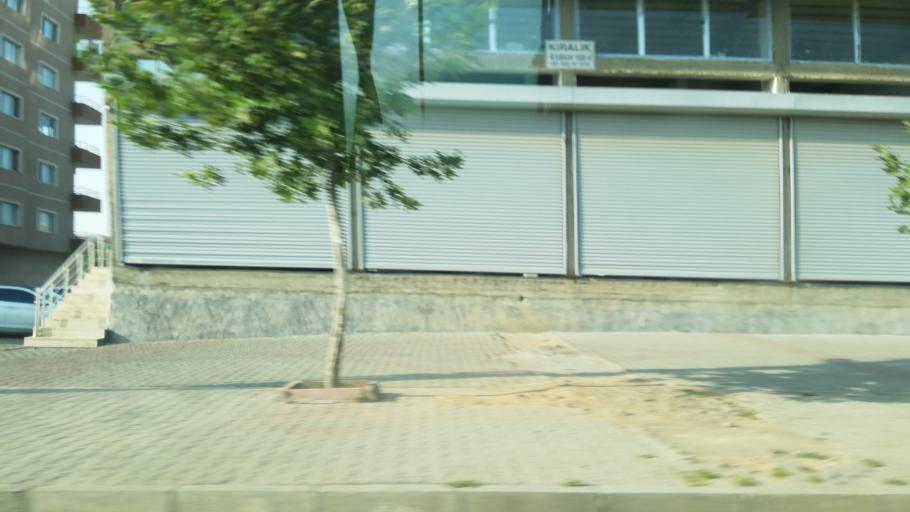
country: TR
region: Mardin
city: Midyat
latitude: 37.4347
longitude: 41.3273
